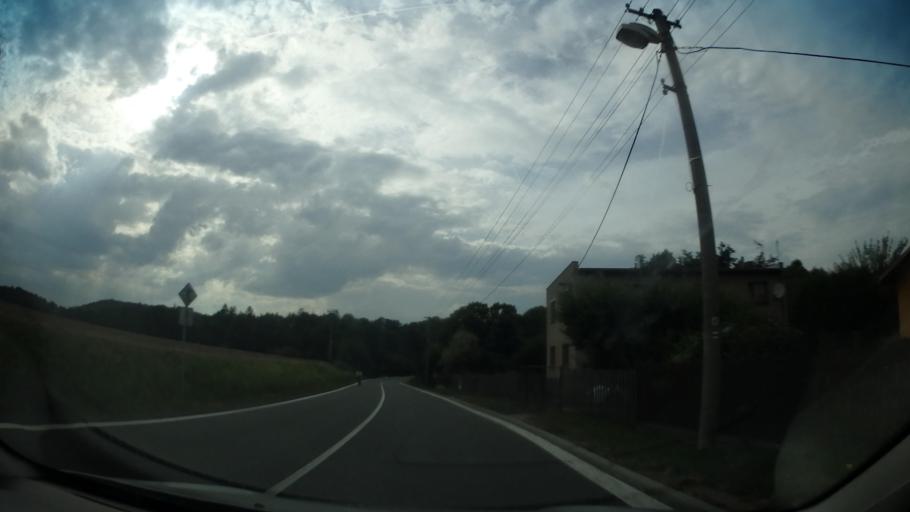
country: CZ
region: Pardubicky
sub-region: Okres Chrudim
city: Tremosnice
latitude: 49.8757
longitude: 15.6057
